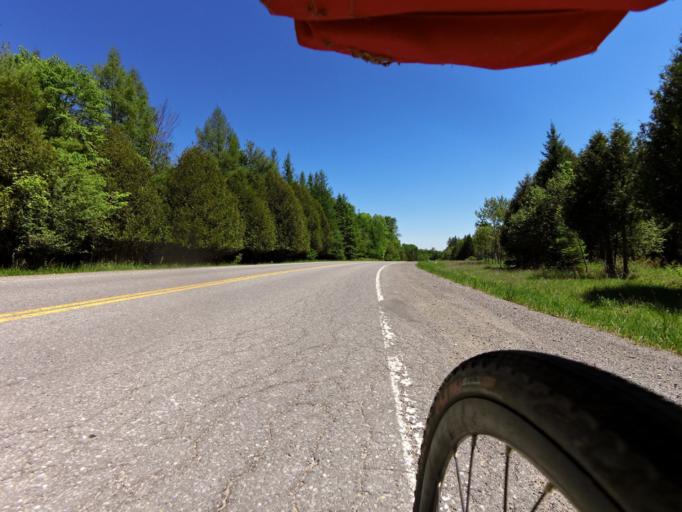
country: CA
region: Ontario
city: Carleton Place
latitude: 45.1844
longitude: -76.3922
